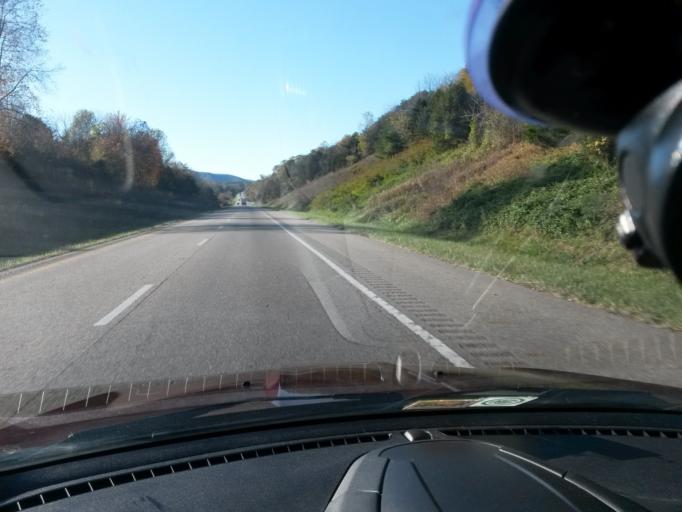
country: US
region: Virginia
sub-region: City of Lexington
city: Lexington
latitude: 37.8694
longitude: -79.5089
